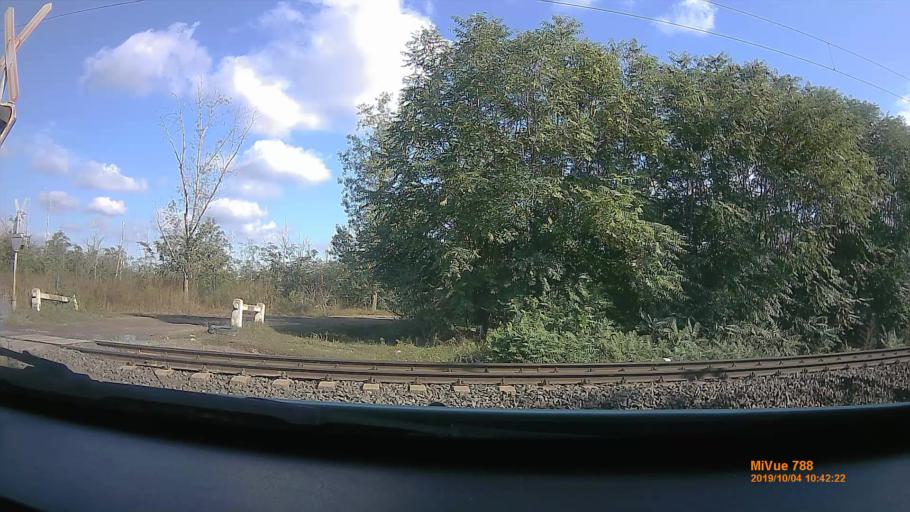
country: HU
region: Szabolcs-Szatmar-Bereg
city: Nyirtelek
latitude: 47.9808
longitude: 21.6630
